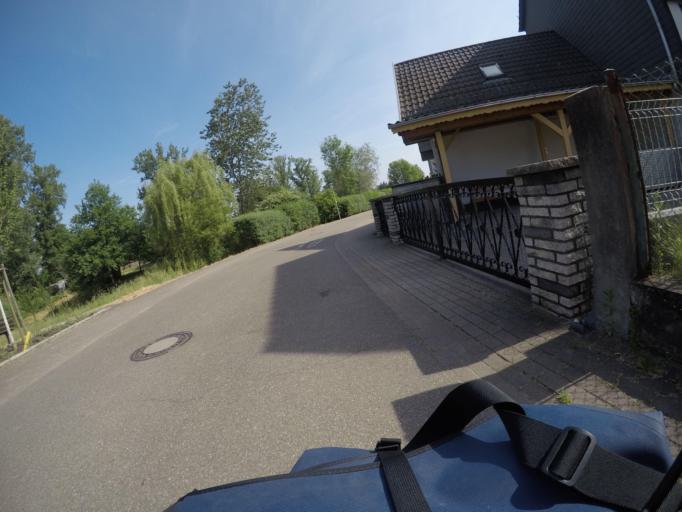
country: DE
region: Baden-Wuerttemberg
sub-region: Karlsruhe Region
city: Bietigheim
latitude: 48.9137
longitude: 8.2408
